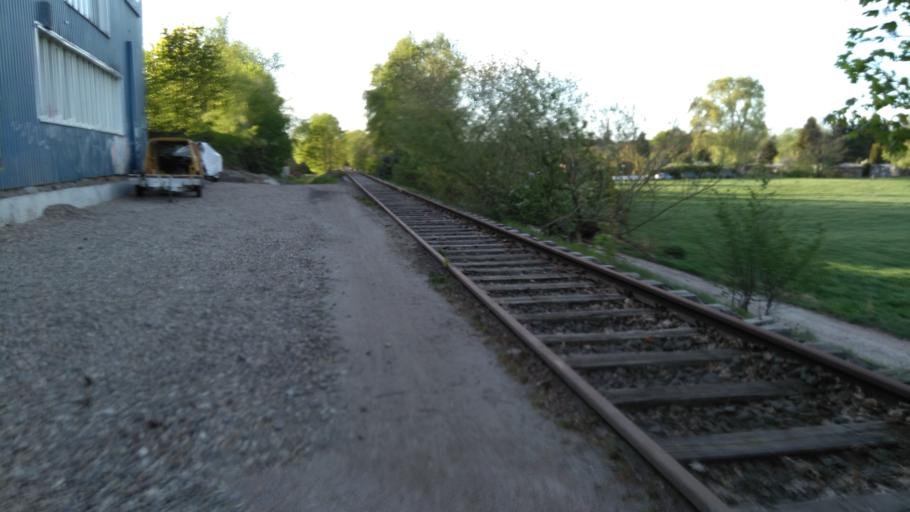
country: DE
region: Lower Saxony
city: Buxtehude
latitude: 53.4662
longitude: 9.7053
